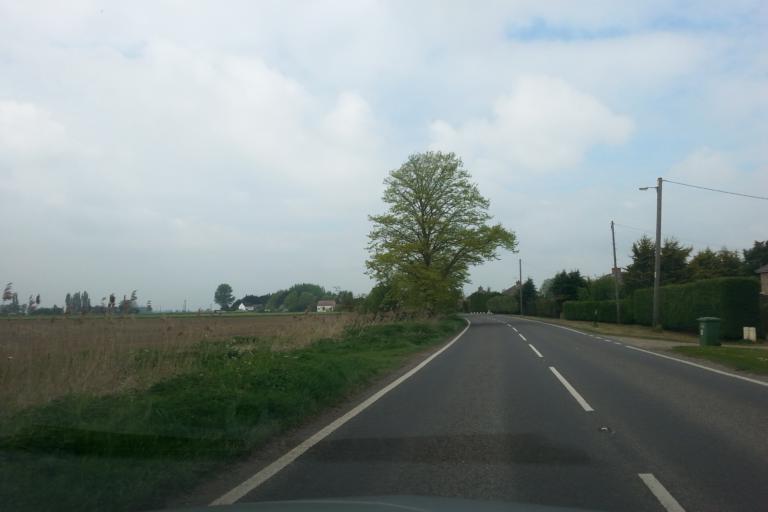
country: GB
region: England
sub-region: Norfolk
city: Outwell
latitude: 52.5716
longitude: 0.2277
